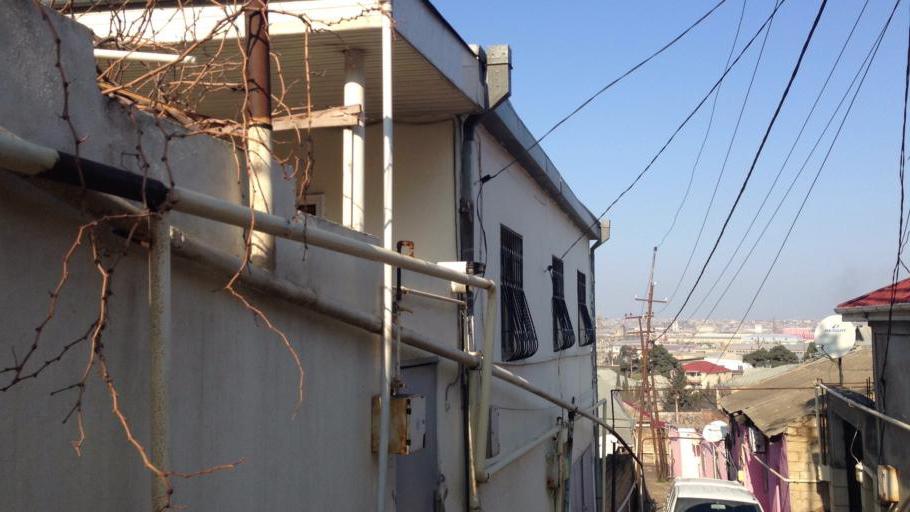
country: AZ
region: Baki
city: Binagadi
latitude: 40.4370
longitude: 49.8526
